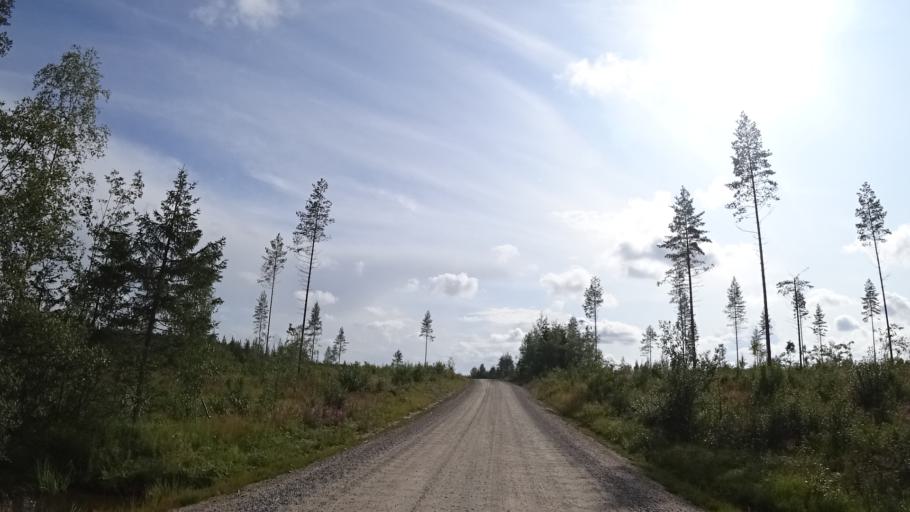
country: FI
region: North Karelia
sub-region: Pielisen Karjala
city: Lieksa
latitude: 63.5857
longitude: 30.1340
